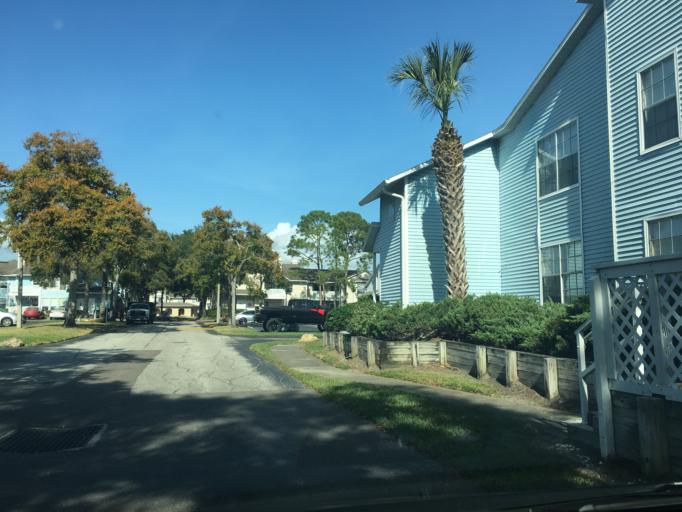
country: US
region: Florida
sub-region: Hillsborough County
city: Town 'n' Country
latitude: 27.9928
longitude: -82.5579
